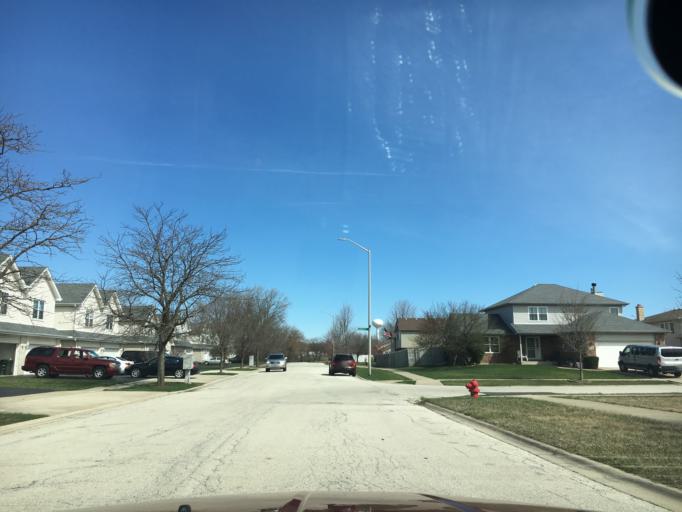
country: US
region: Illinois
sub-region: Cook County
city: Oak Forest
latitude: 41.5901
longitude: -87.7345
